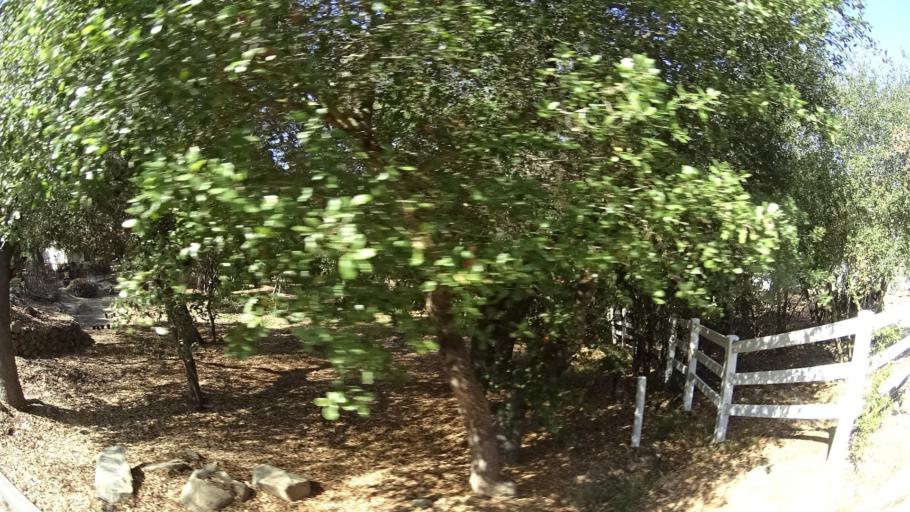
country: US
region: California
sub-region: San Diego County
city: Rancho Santa Fe
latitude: 33.0621
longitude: -117.1386
